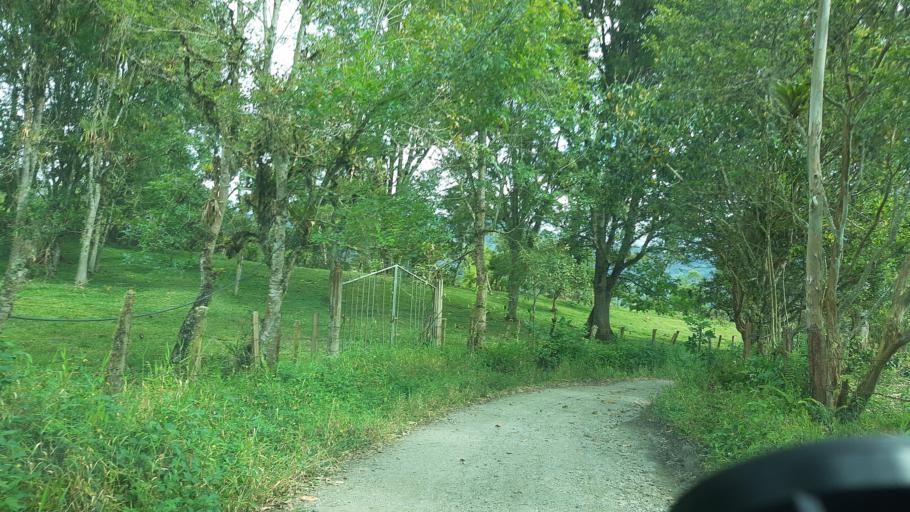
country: CO
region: Boyaca
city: Garagoa
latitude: 5.0436
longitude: -73.3454
